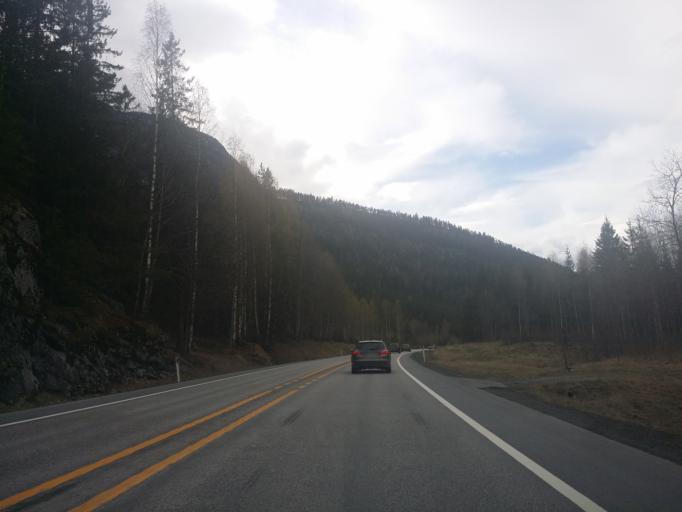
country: NO
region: Buskerud
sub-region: Fla
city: Fla
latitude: 60.4452
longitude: 9.2839
